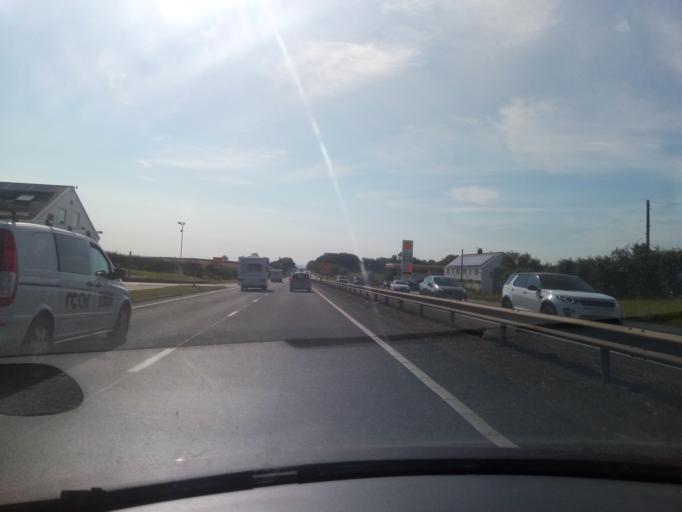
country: GB
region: England
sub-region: Hartlepool
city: Elwick
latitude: 54.6549
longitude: -1.3034
